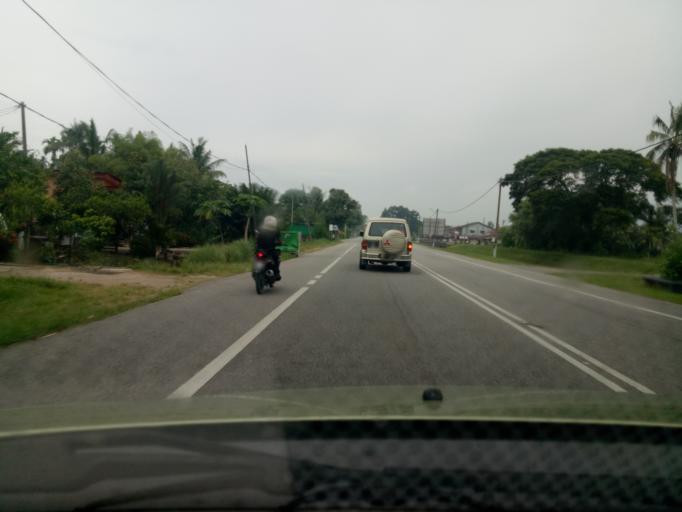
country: MY
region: Kedah
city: Gurun
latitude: 5.8880
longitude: 100.4429
